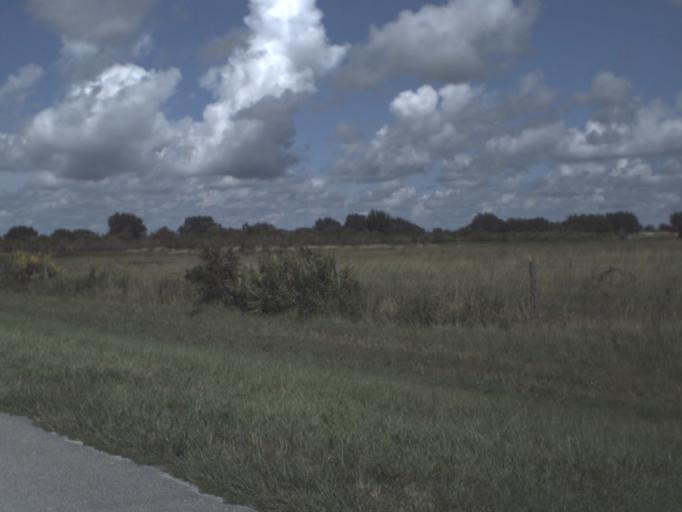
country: US
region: Florida
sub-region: Highlands County
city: Lake Placid
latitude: 27.4122
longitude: -81.1884
